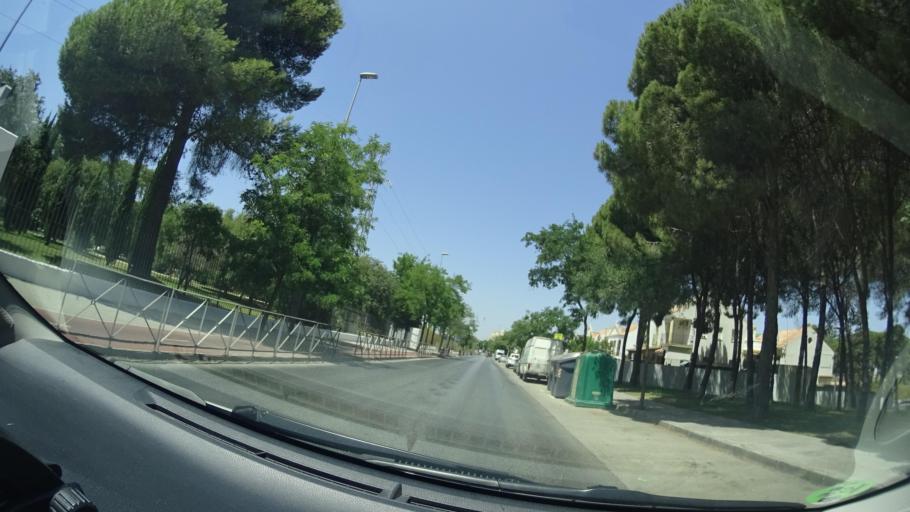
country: ES
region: Andalusia
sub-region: Provincia de Cadiz
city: Jerez de la Frontera
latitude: 36.6739
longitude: -6.1225
